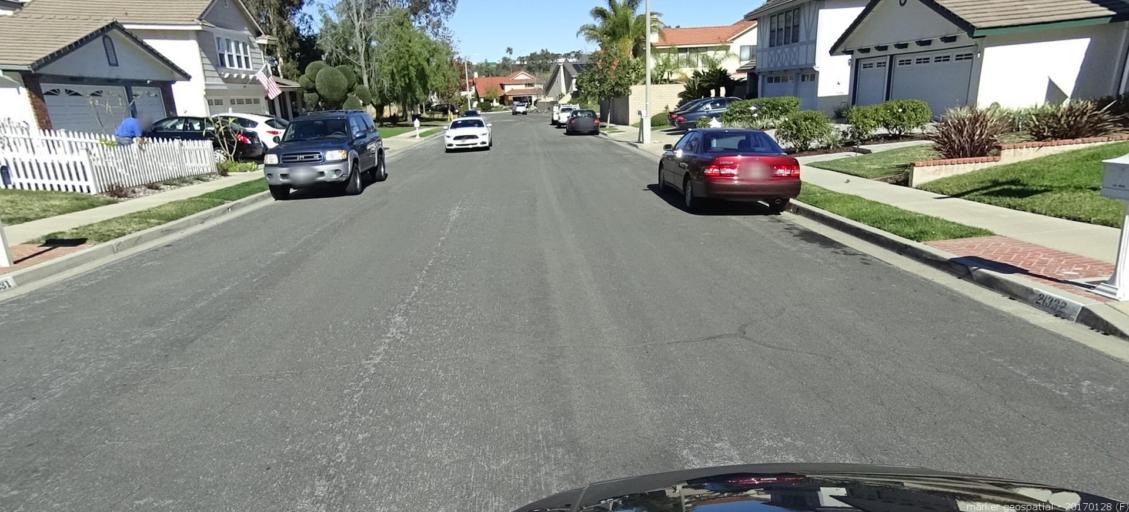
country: US
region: California
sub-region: Orange County
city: Lake Forest
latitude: 33.6532
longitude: -117.6913
